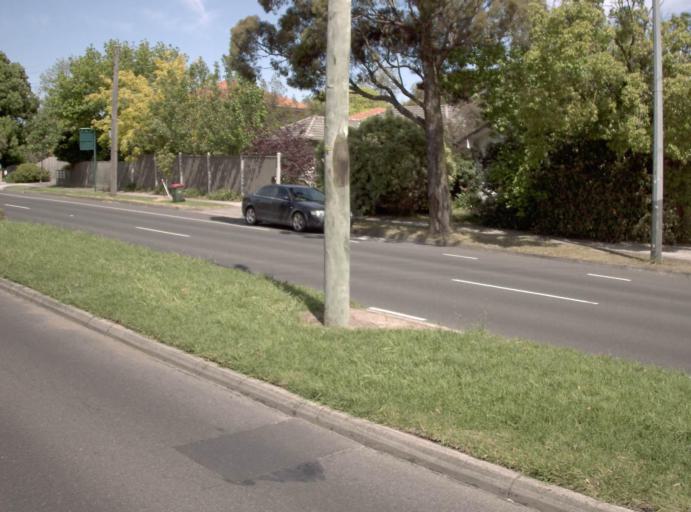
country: AU
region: Victoria
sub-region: Whitehorse
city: Blackburn South
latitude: -37.8414
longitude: 145.1554
